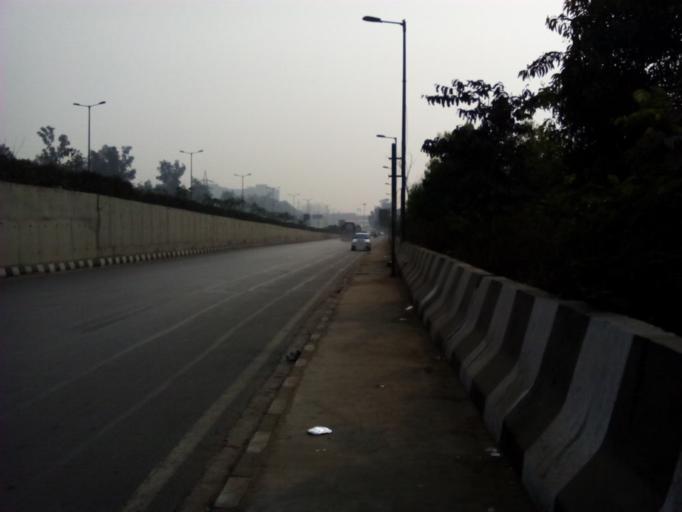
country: IN
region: Uttar Pradesh
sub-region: Gautam Buddha Nagar
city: Noida
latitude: 28.6515
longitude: 77.3191
